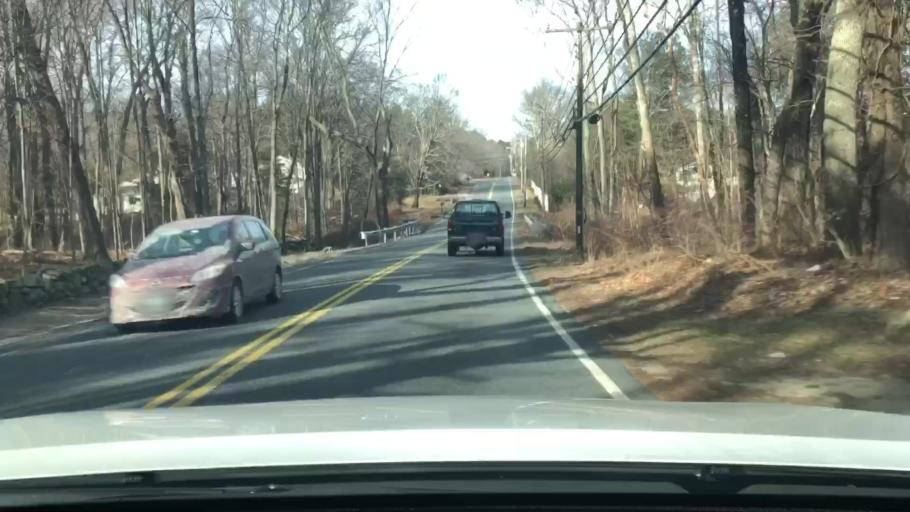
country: US
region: Massachusetts
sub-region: Worcester County
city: Mendon
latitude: 42.0873
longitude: -71.5316
